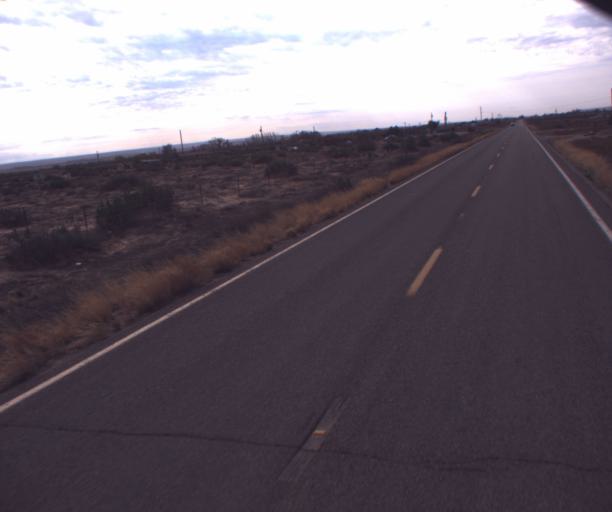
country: US
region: Arizona
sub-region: Apache County
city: Many Farms
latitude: 36.4398
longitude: -109.6073
